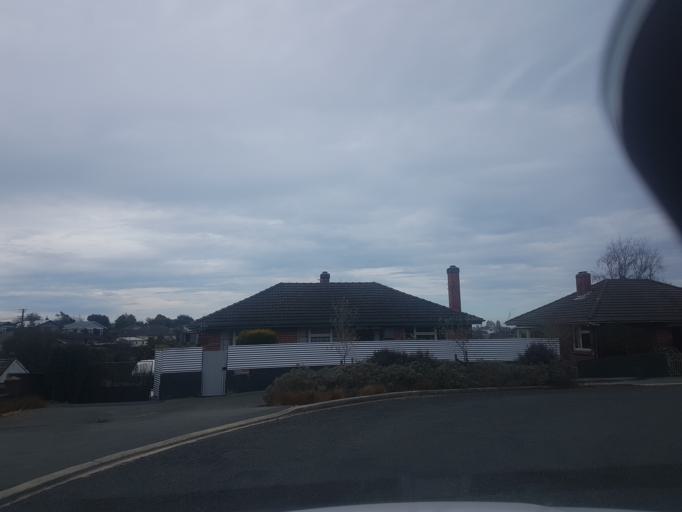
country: NZ
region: Canterbury
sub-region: Timaru District
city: Timaru
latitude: -44.4035
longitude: 171.2339
